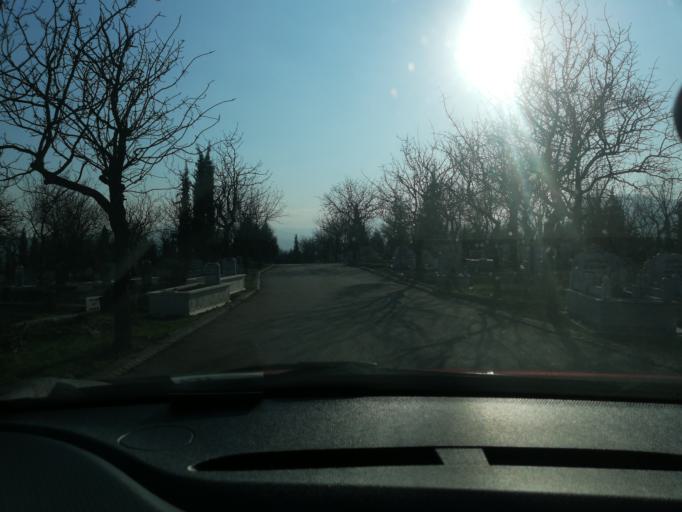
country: TR
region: Karabuk
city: Safranbolu
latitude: 41.2412
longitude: 32.6956
